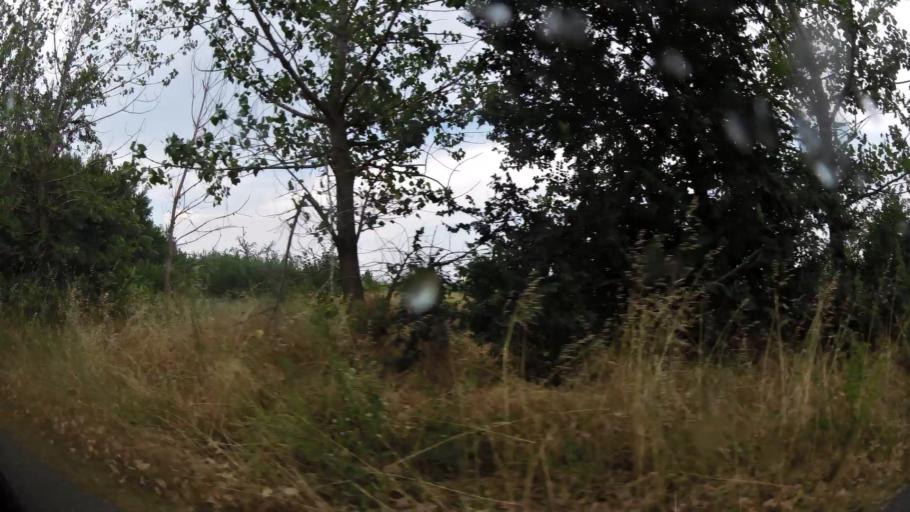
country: GR
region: Central Macedonia
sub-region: Nomos Pierias
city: Paralia
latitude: 40.2809
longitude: 22.6014
